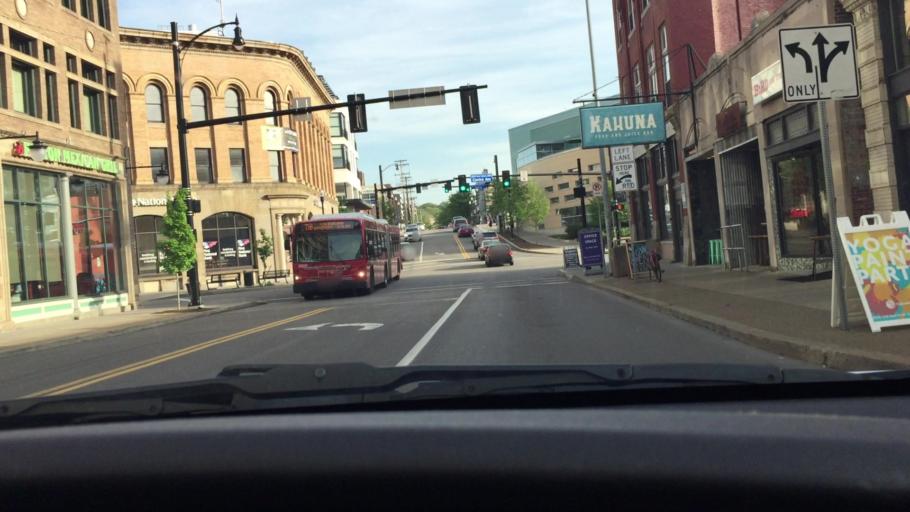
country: US
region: Pennsylvania
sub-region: Allegheny County
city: Bloomfield
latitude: 40.4604
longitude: -79.9251
